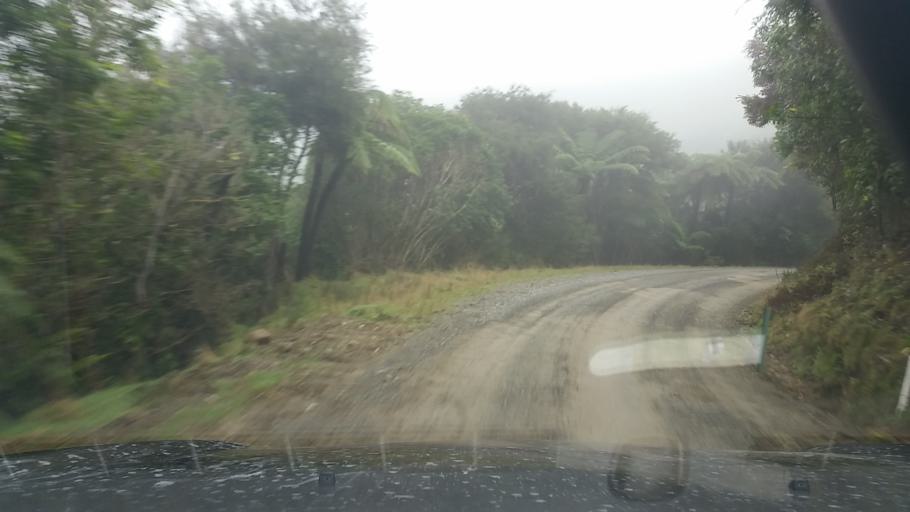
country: NZ
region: Marlborough
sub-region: Marlborough District
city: Picton
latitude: -41.1785
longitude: 173.9829
